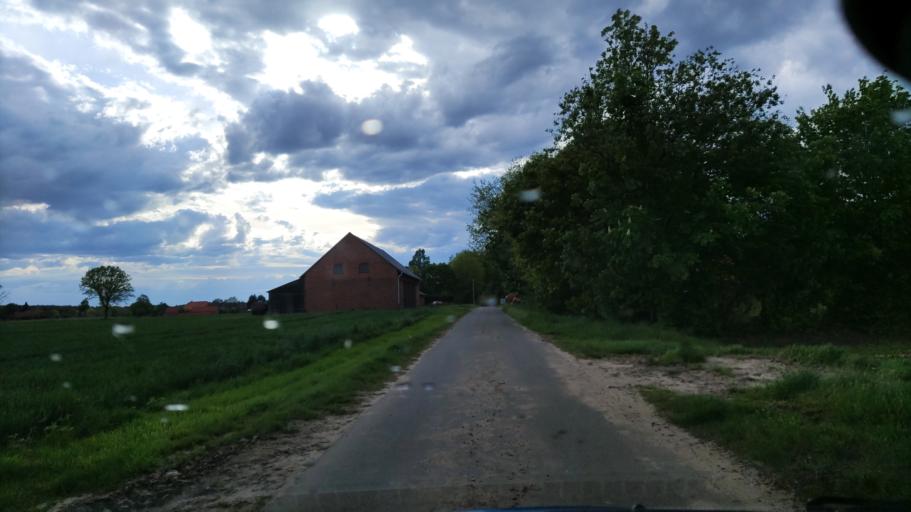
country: DE
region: Lower Saxony
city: Dahlenburg
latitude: 53.1758
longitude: 10.7185
